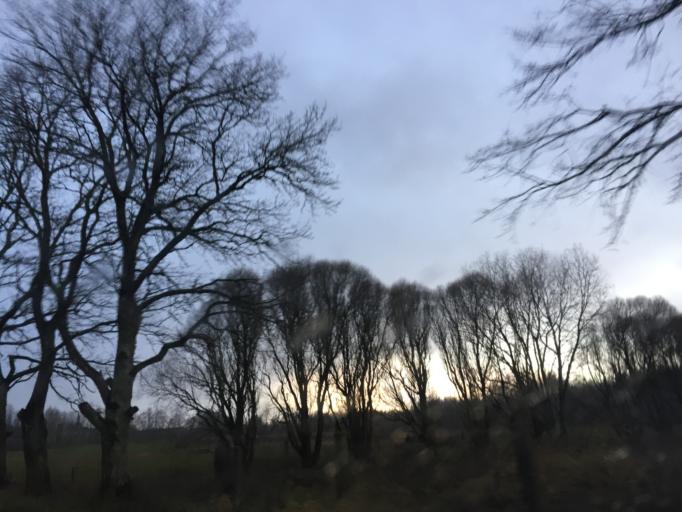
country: LV
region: Burtnieki
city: Matisi
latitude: 57.6961
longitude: 25.2661
